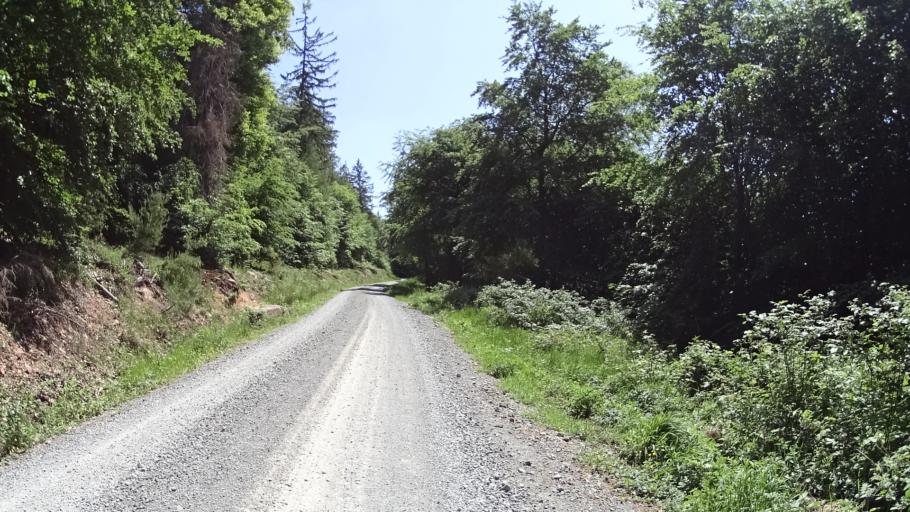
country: DE
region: Baden-Wuerttemberg
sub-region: Karlsruhe Region
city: Schonau
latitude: 49.4255
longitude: 8.7881
